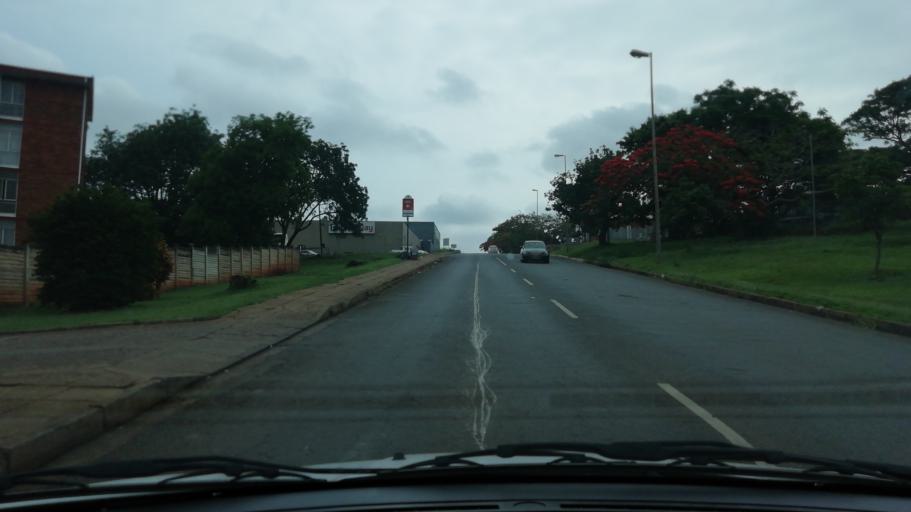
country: ZA
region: KwaZulu-Natal
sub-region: uThungulu District Municipality
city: Empangeni
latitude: -28.7387
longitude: 31.8915
